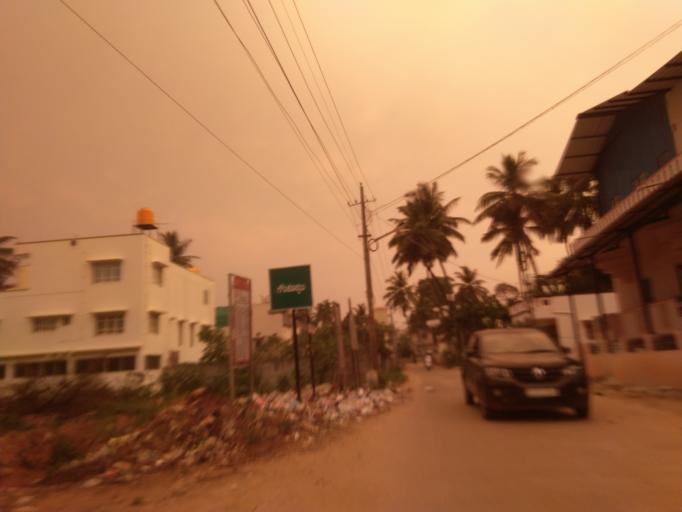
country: IN
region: Karnataka
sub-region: Hassan
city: Hassan
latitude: 13.0138
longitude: 76.1095
